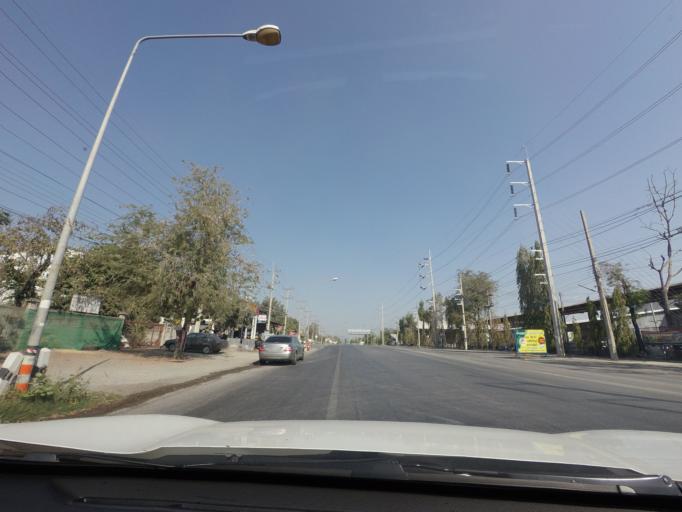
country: TH
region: Nakhon Ratchasima
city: Pak Chong
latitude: 14.6780
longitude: 101.4539
